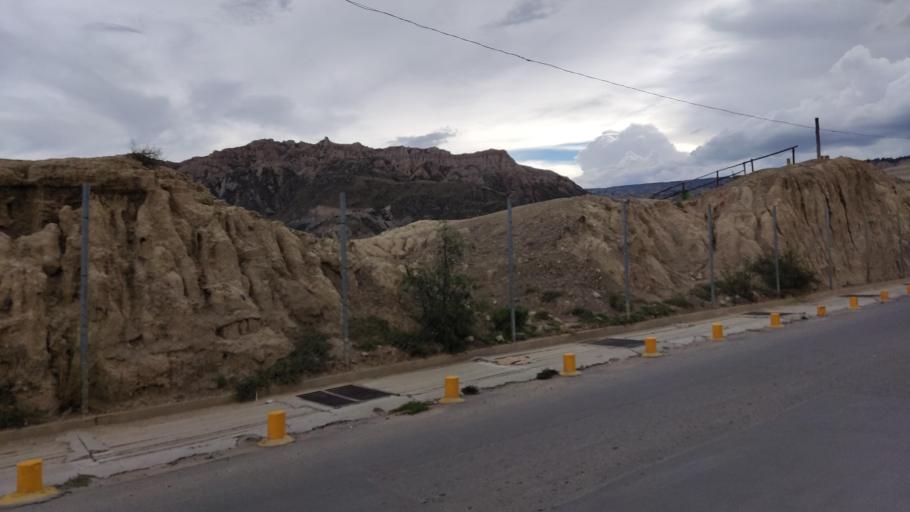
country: BO
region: La Paz
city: La Paz
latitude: -16.5673
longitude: -68.0923
